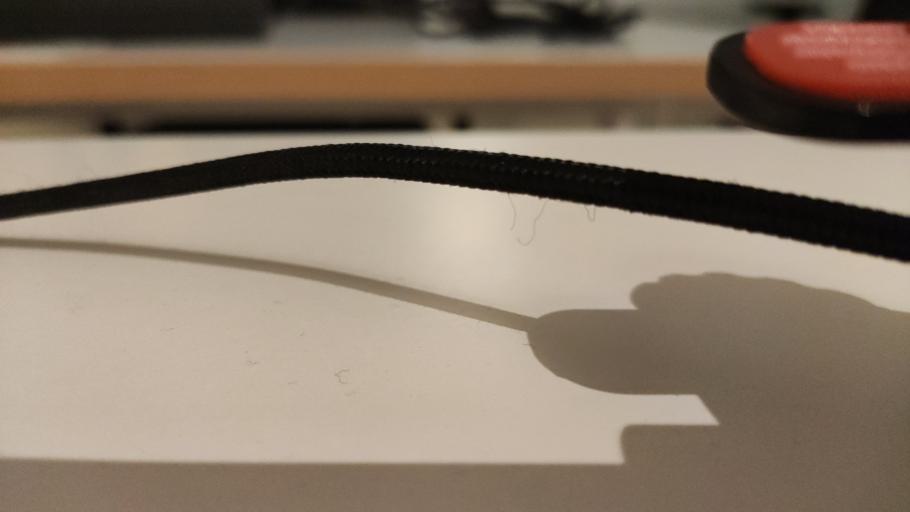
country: RU
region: Moskovskaya
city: Il'inskiy Pogost
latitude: 55.5253
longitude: 38.8721
